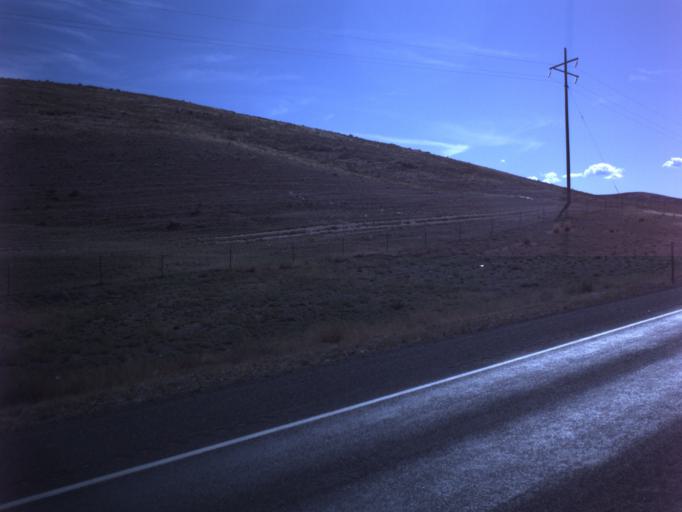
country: US
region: Utah
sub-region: Sanpete County
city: Gunnison
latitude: 39.2041
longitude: -111.8475
